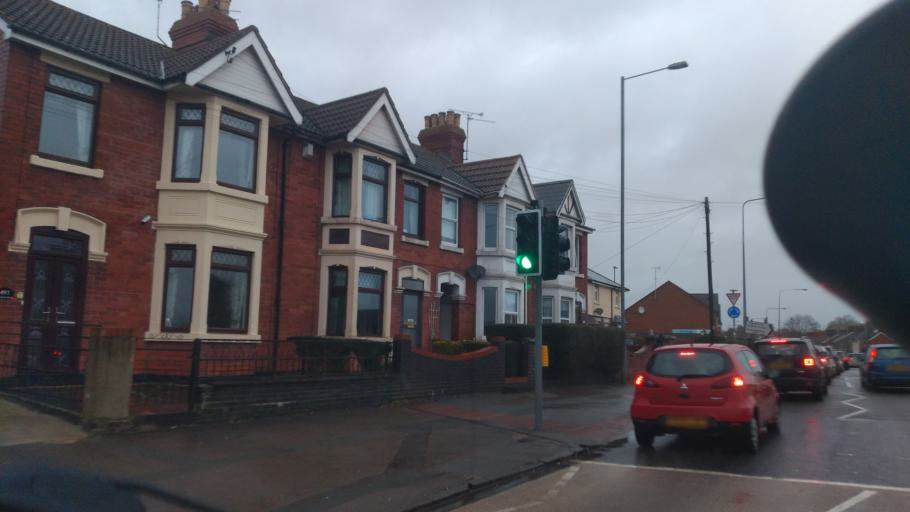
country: GB
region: England
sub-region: Borough of Swindon
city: Swindon
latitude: 51.5827
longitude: -1.7753
